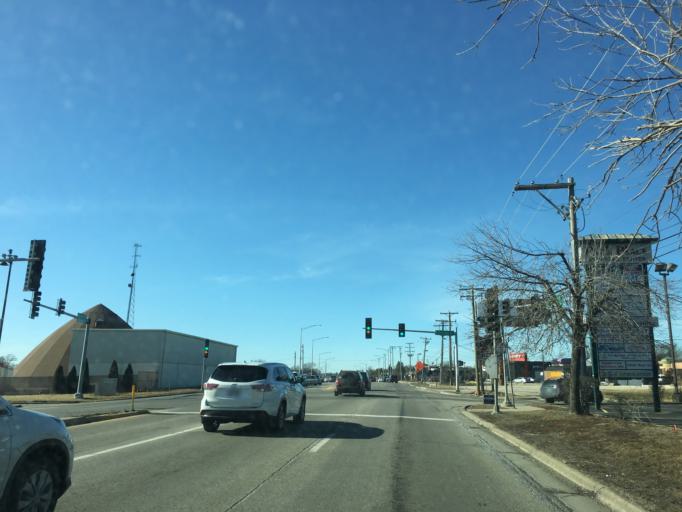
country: US
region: Illinois
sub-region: Cook County
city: Rolling Meadows
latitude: 42.0669
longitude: -88.0396
